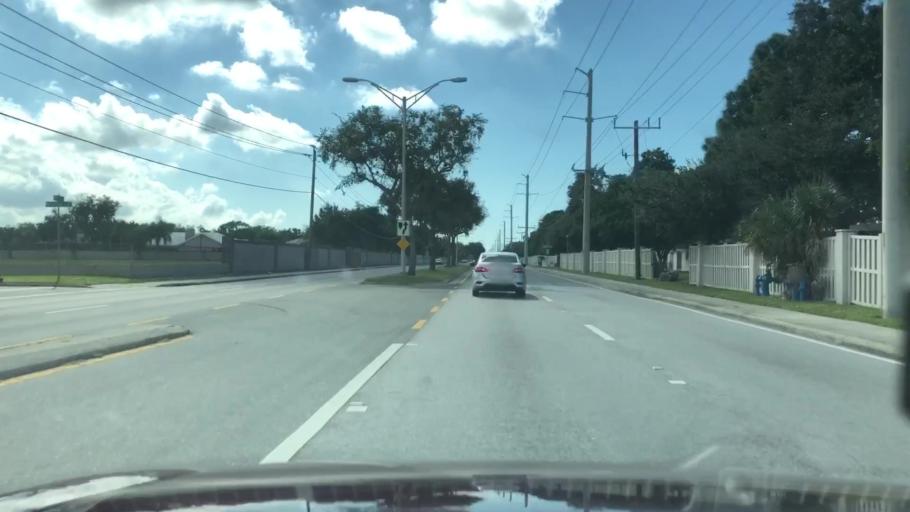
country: US
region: Florida
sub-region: Sarasota County
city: Gulf Gate Estates
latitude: 27.2640
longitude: -82.4977
